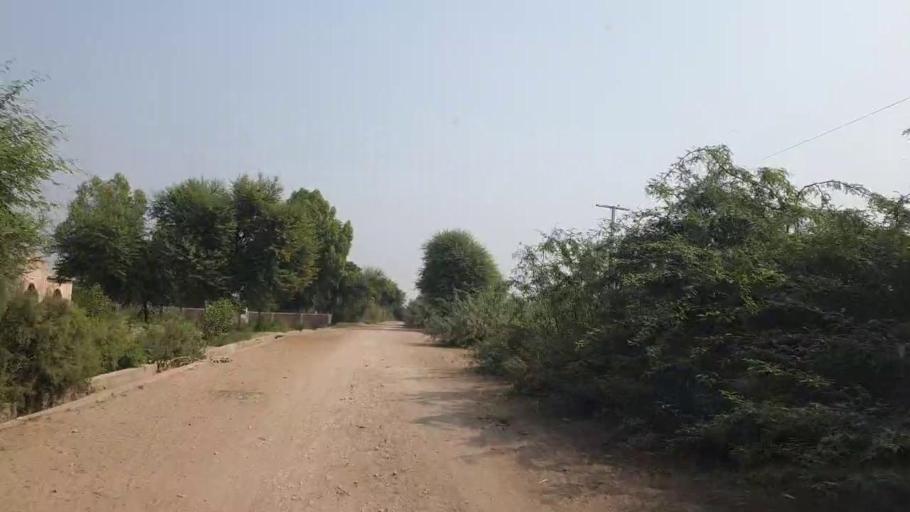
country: PK
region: Sindh
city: Tando Ghulam Ali
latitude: 25.1702
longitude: 68.7289
